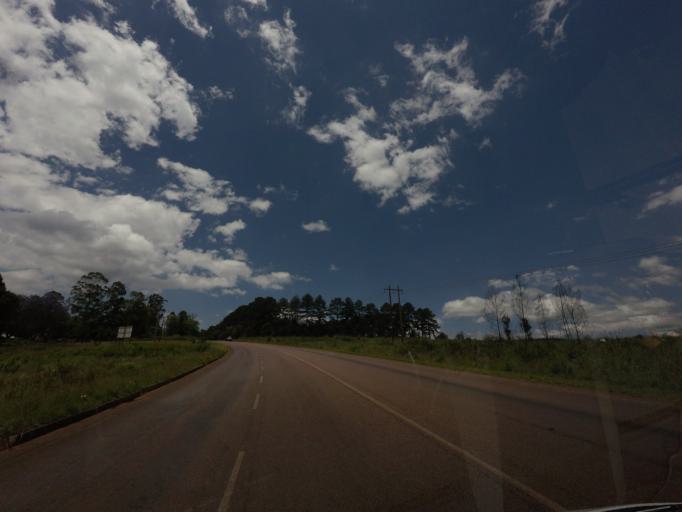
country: ZA
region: Mpumalanga
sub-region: Ehlanzeni District
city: Graksop
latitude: -25.0862
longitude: 30.7834
